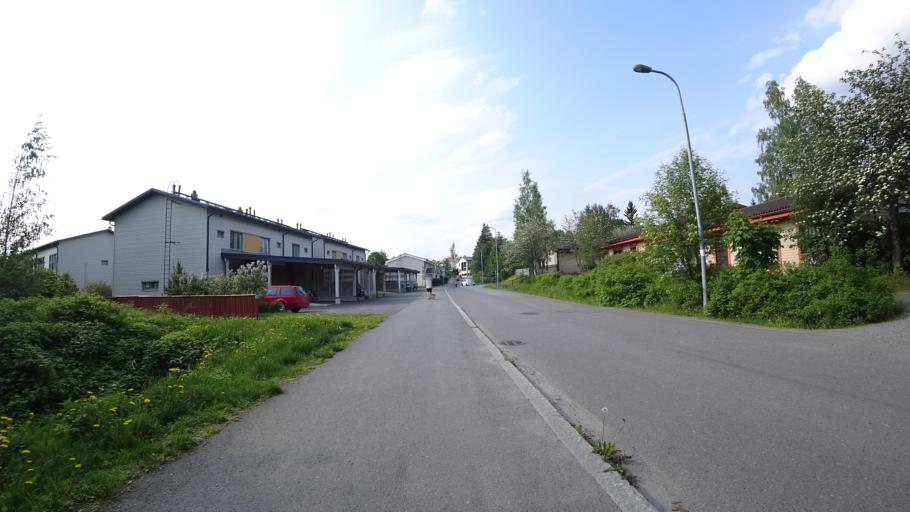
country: FI
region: Pirkanmaa
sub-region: Tampere
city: Pirkkala
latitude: 61.5030
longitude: 23.6888
